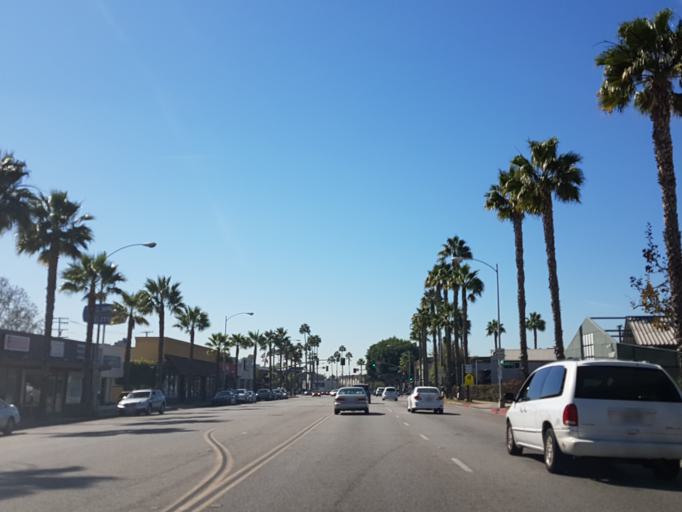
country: US
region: California
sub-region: Los Angeles County
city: Culver City
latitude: 34.0147
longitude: -118.4079
